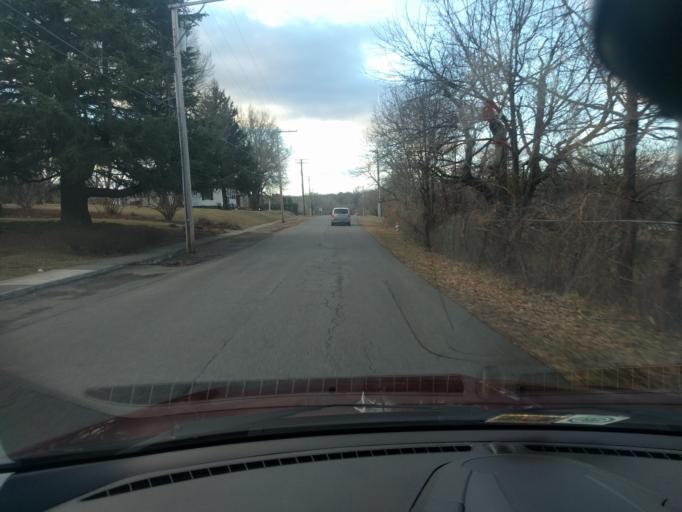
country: US
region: Virginia
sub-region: City of Bedford
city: Bedford
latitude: 37.3391
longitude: -79.5289
